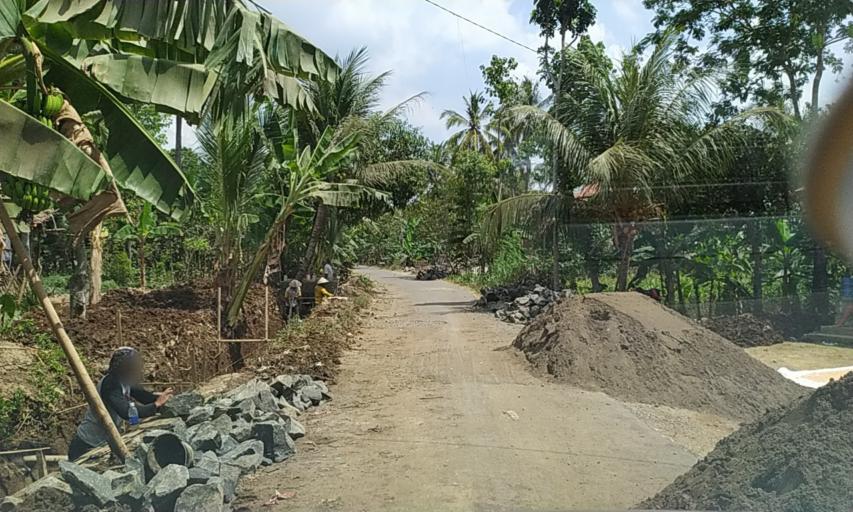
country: ID
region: Central Java
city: Tawangsari
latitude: -7.3913
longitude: 108.7952
